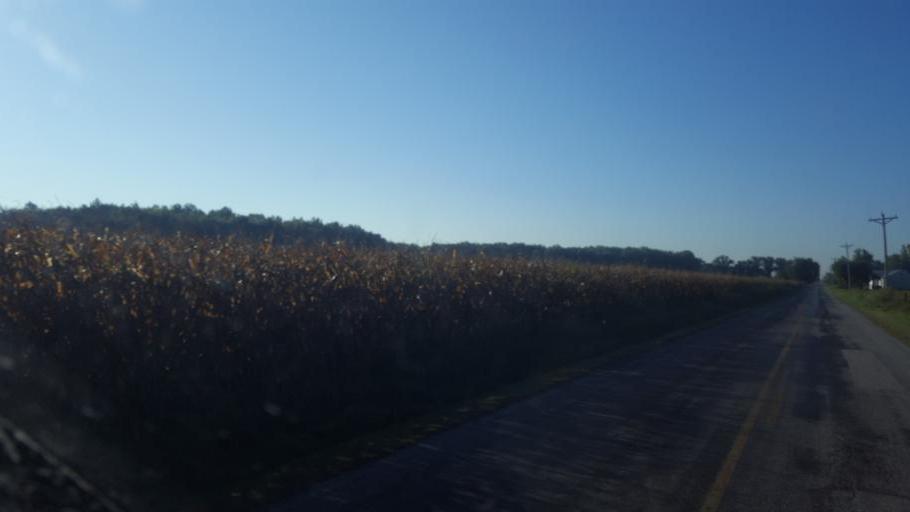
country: US
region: Ohio
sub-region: Morrow County
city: Cardington
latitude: 40.5537
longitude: -82.9956
